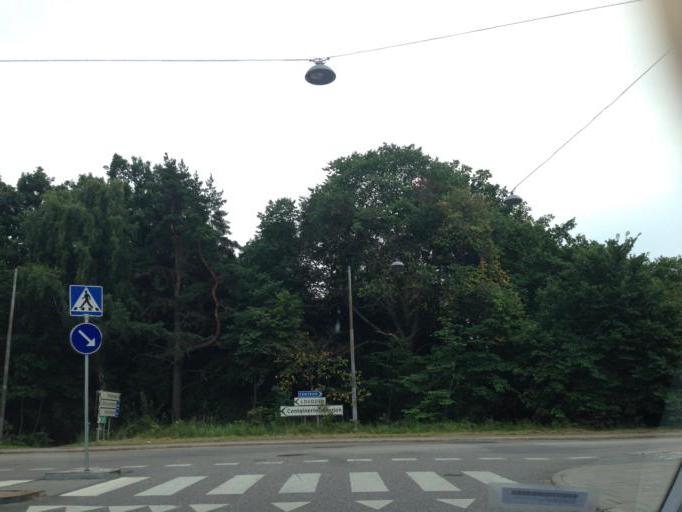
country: SE
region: Stockholm
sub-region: Stockholms Kommun
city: OEstermalm
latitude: 59.3397
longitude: 18.1144
